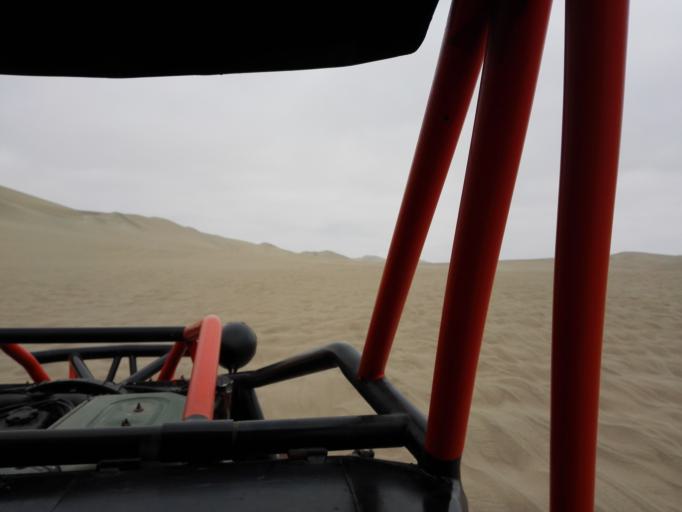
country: PE
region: Ica
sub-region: Provincia de Ica
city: Ica
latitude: -14.0874
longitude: -75.7695
